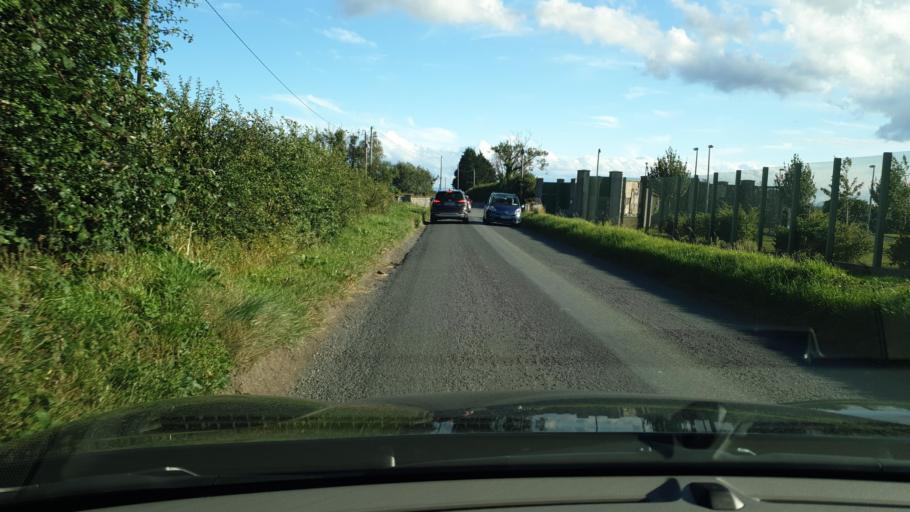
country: IE
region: Leinster
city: Lusk
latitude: 53.5519
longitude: -6.1888
